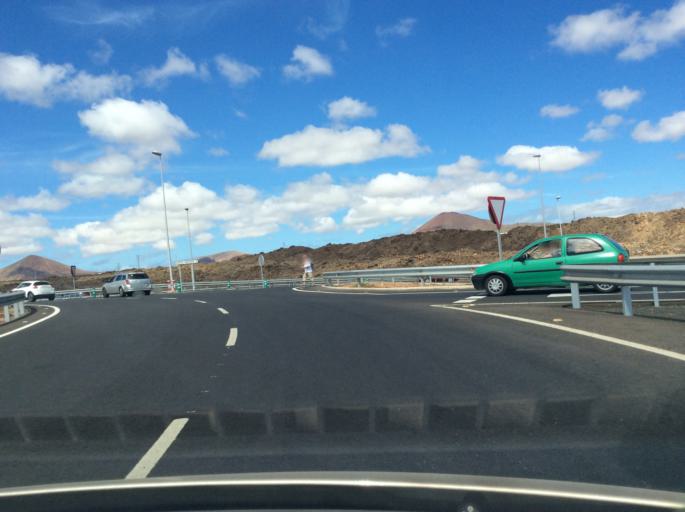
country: ES
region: Canary Islands
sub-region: Provincia de Las Palmas
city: Arrecife
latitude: 28.9774
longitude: -13.5304
